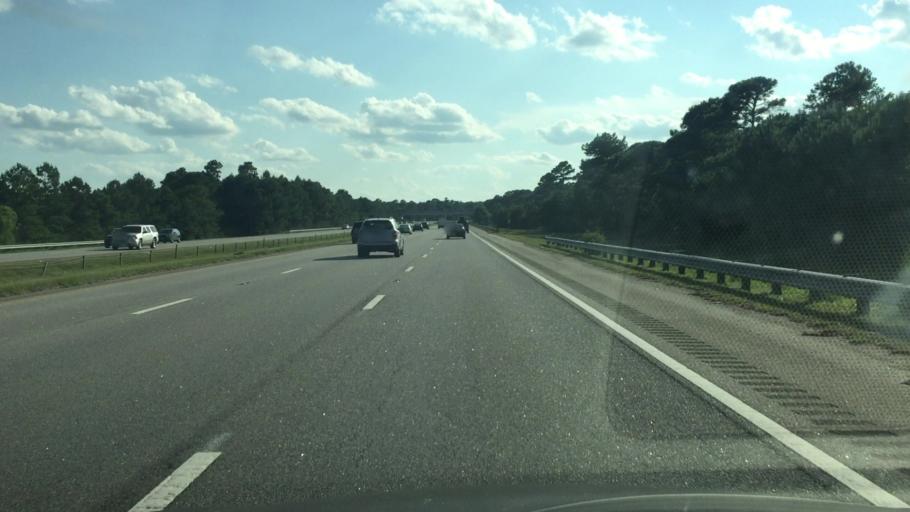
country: US
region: South Carolina
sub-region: Horry County
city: North Myrtle Beach
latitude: 33.8302
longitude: -78.7191
